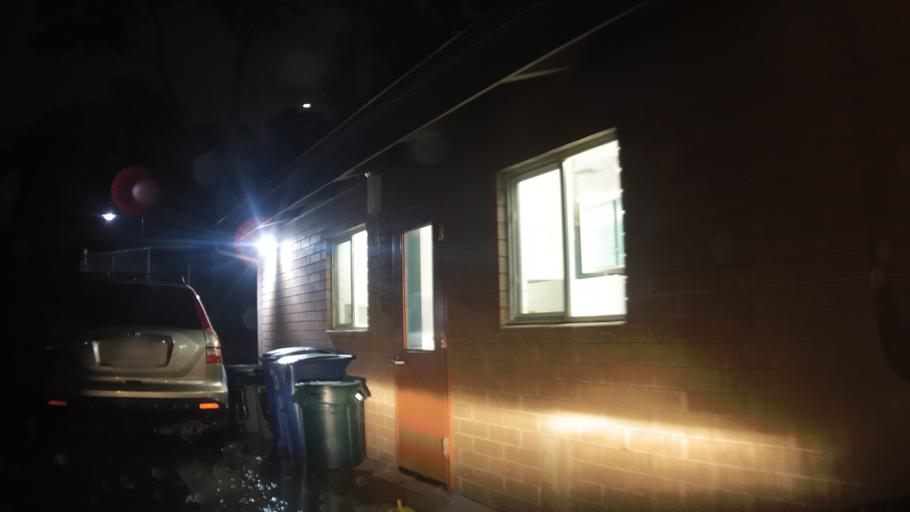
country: US
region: California
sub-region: San Diego County
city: San Diego
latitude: 32.7390
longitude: -117.1532
